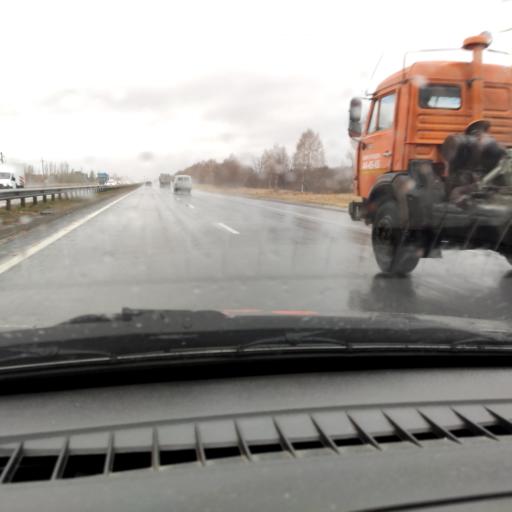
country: RU
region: Samara
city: Tol'yatti
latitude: 53.5761
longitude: 49.4334
